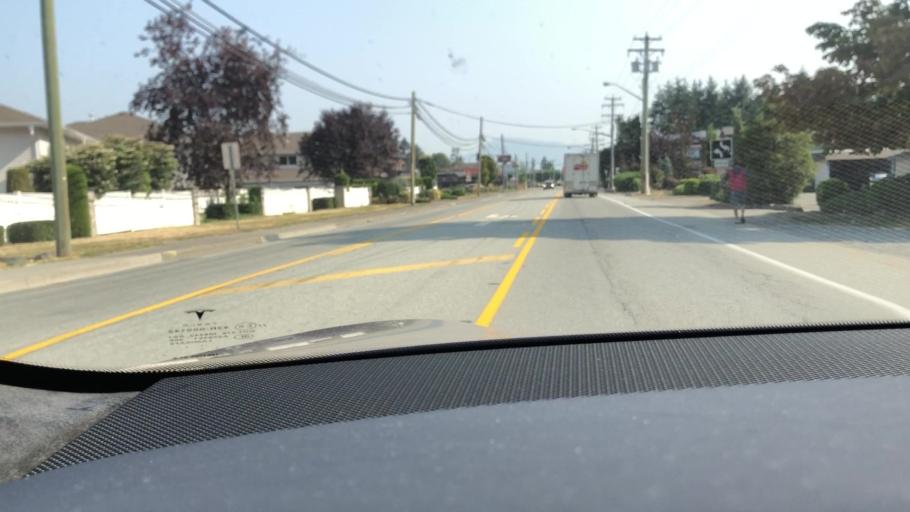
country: CA
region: British Columbia
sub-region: Fraser Valley Regional District
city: Chilliwack
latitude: 49.1073
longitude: -121.9599
